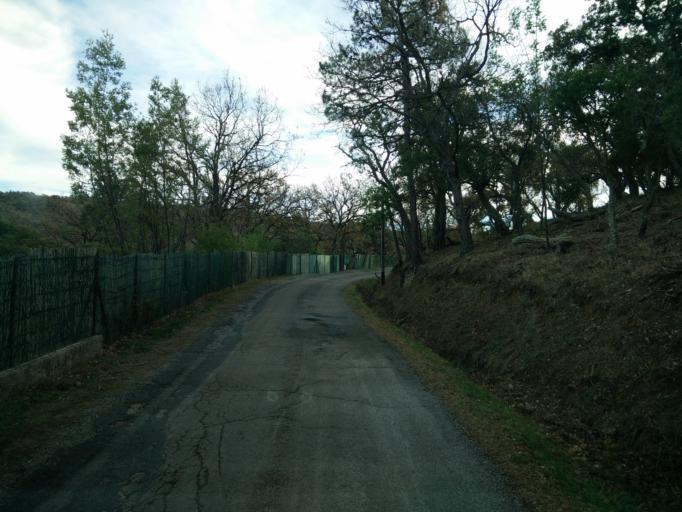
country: FR
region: Provence-Alpes-Cote d'Azur
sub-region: Departement du Var
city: Roquebrune-sur-Argens
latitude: 43.4298
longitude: 6.6388
